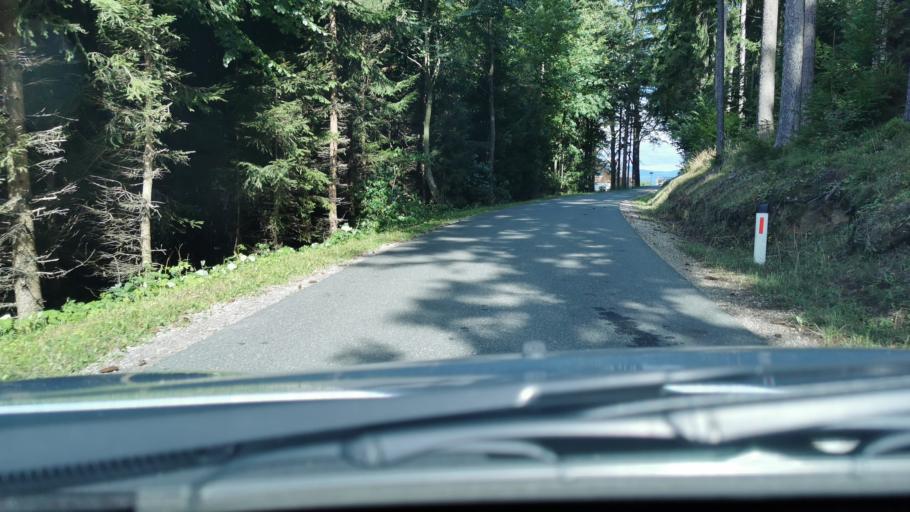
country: AT
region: Styria
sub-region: Politischer Bezirk Weiz
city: Koglhof
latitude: 47.3168
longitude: 15.7065
